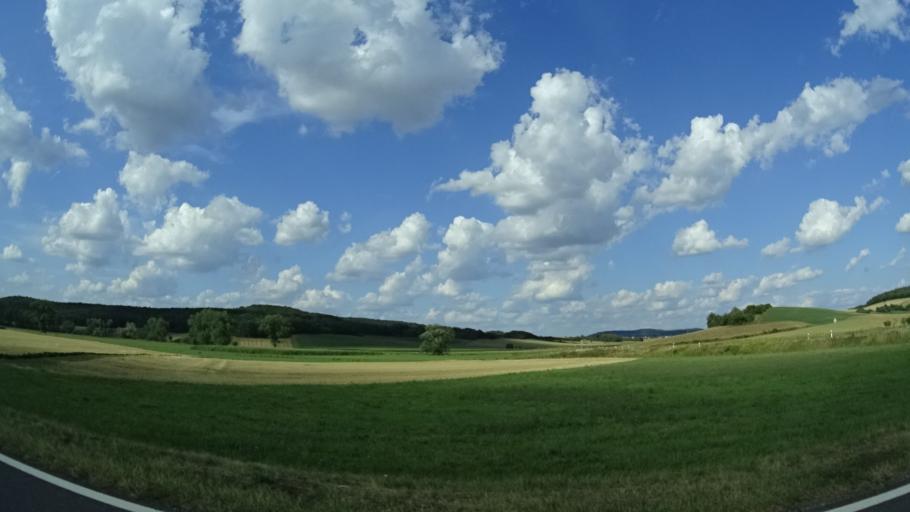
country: DE
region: Bavaria
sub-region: Regierungsbezirk Unterfranken
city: Bad Konigshofen im Grabfeld
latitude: 50.2787
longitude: 10.5221
